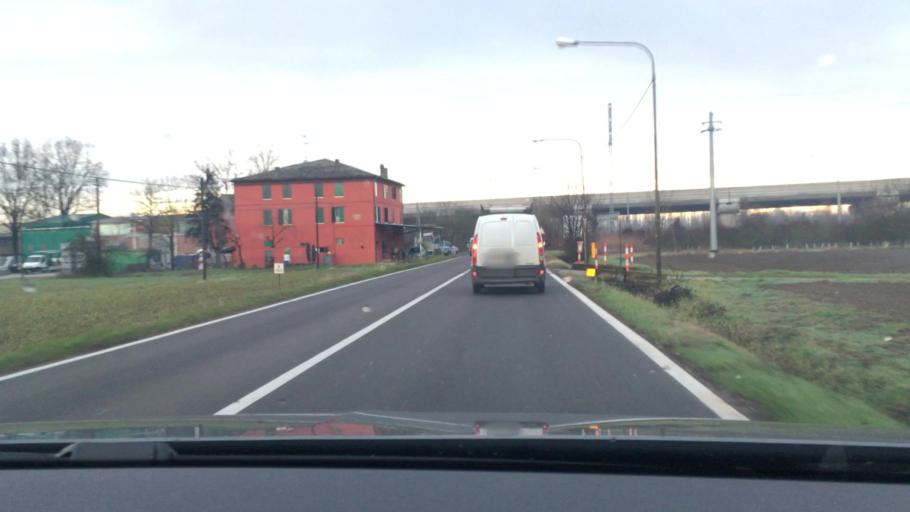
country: IT
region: Emilia-Romagna
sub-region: Provincia di Modena
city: Albareto
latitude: 44.6930
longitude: 10.9447
